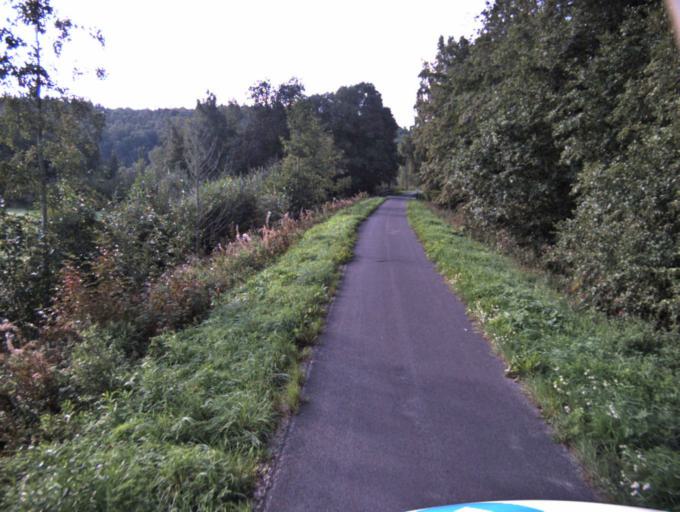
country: SE
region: Vaestra Goetaland
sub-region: Ulricehamns Kommun
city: Ulricehamn
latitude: 57.7331
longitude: 13.4096
